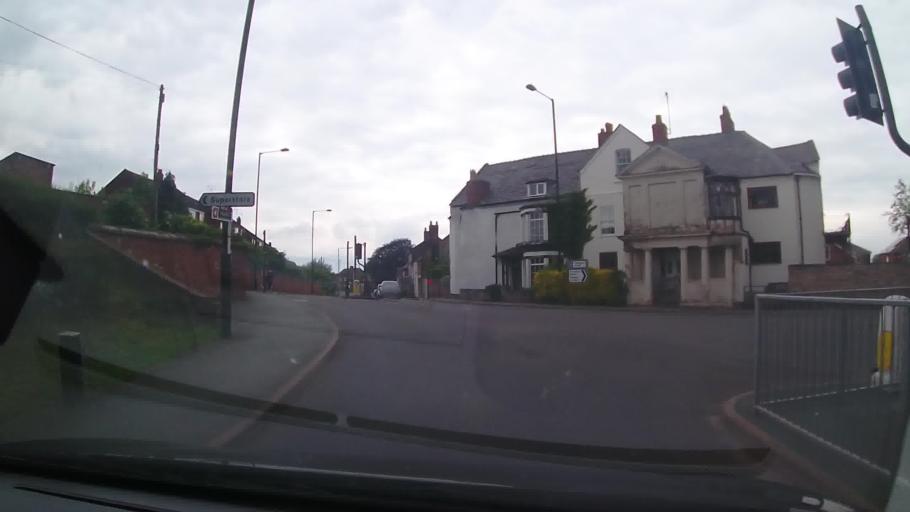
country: GB
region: England
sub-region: Shropshire
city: Ellesmere
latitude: 52.9055
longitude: -2.8986
